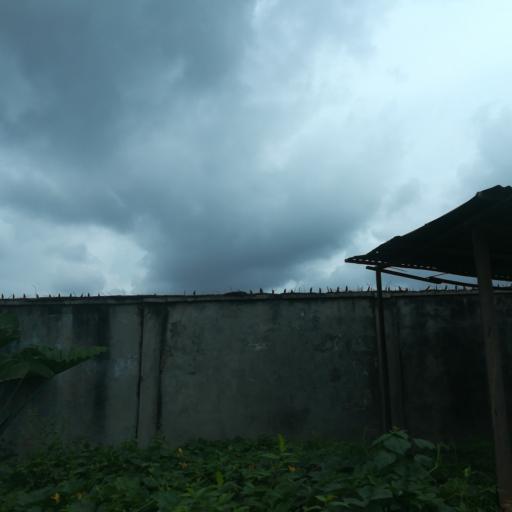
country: NG
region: Rivers
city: Port Harcourt
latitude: 4.8290
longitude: 7.0404
